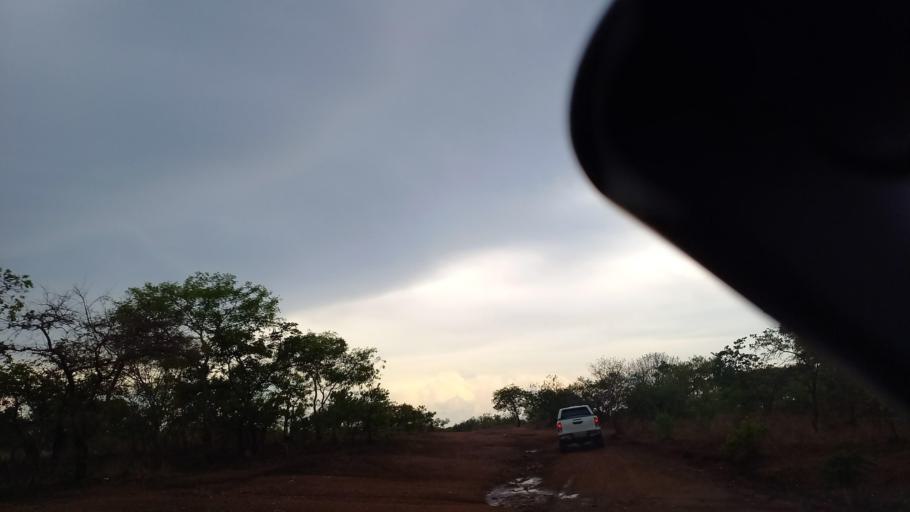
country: ZM
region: Lusaka
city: Kafue
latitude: -16.0219
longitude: 28.2949
